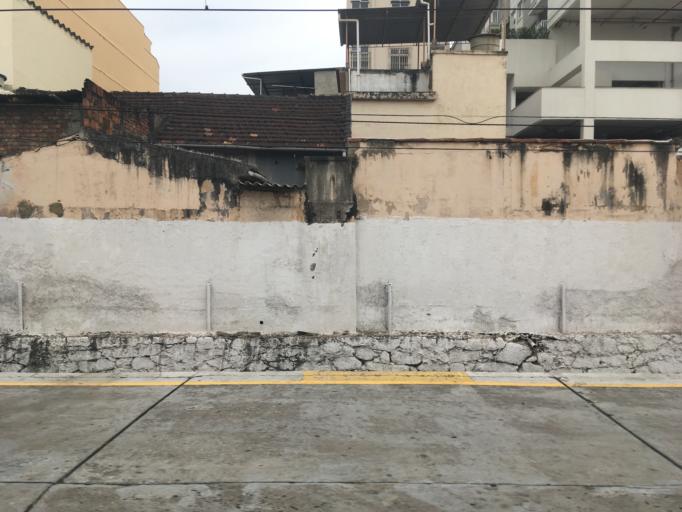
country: BR
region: Rio de Janeiro
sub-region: Rio De Janeiro
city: Rio de Janeiro
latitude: -22.9013
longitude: -43.2554
